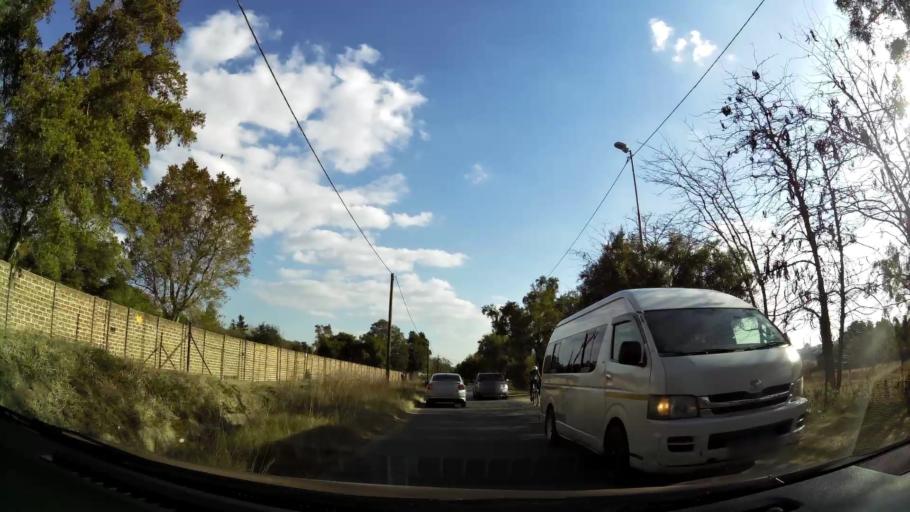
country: ZA
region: Gauteng
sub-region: City of Johannesburg Metropolitan Municipality
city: Midrand
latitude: -26.0195
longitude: 28.1493
